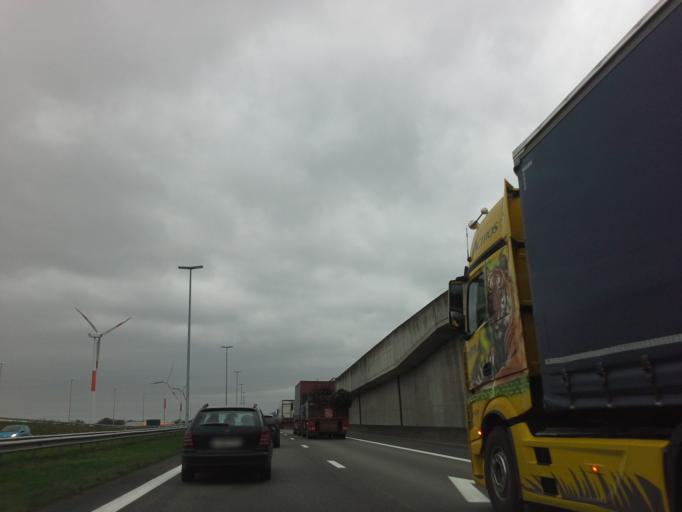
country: NL
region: North Brabant
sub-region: Gemeente Zundert
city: Zundert
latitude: 51.4773
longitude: 4.7308
